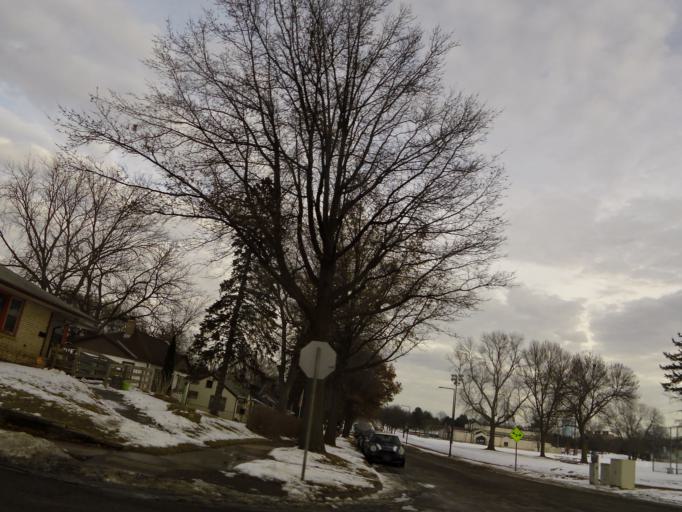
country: US
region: Minnesota
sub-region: Ramsey County
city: Maplewood
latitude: 44.9560
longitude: -93.0151
